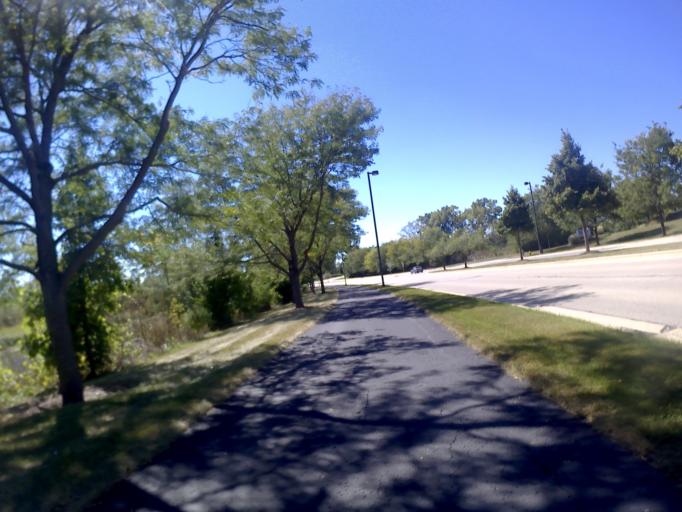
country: US
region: Illinois
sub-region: Cook County
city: Lemont
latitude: 41.6961
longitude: -88.0238
